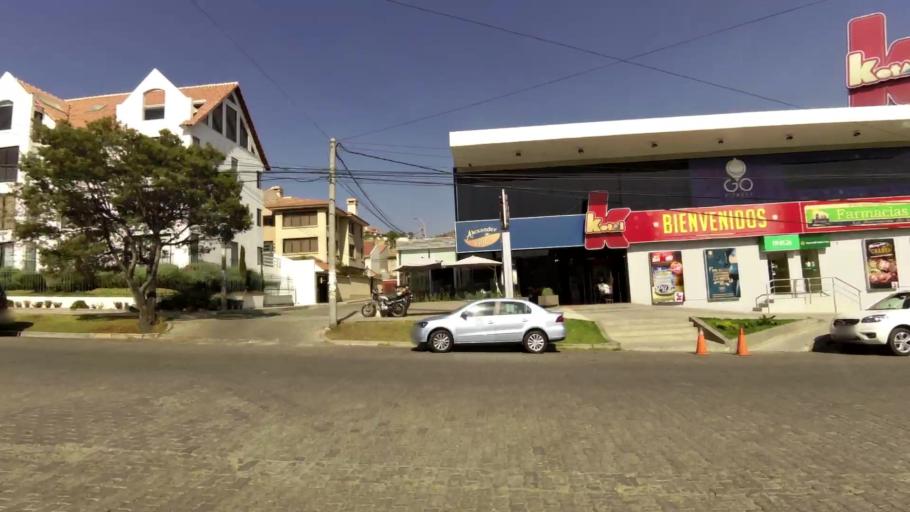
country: BO
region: La Paz
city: La Paz
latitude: -16.5343
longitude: -68.0721
